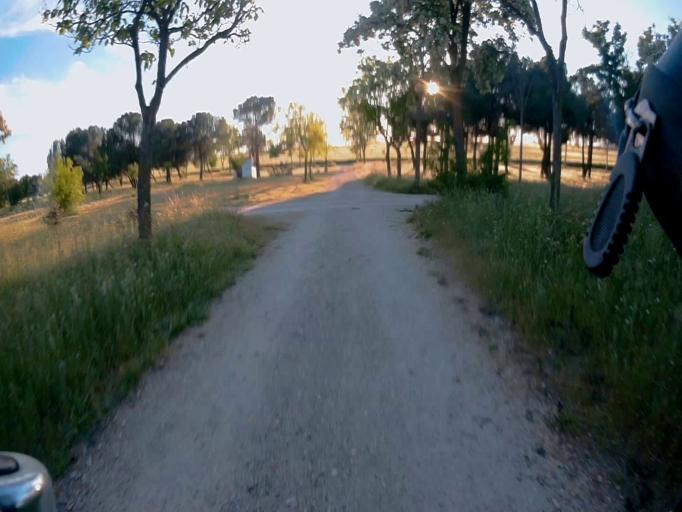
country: ES
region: Madrid
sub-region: Provincia de Madrid
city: Alcorcon
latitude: 40.3200
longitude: -3.8011
